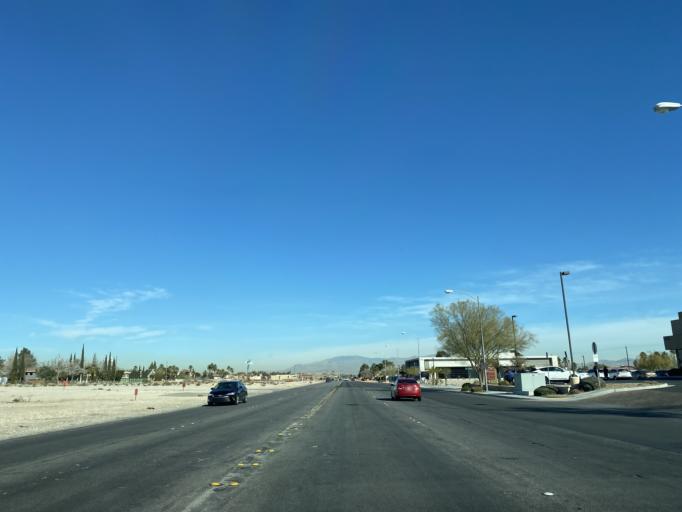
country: US
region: Nevada
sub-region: Clark County
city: Spring Valley
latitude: 36.0792
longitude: -115.2249
